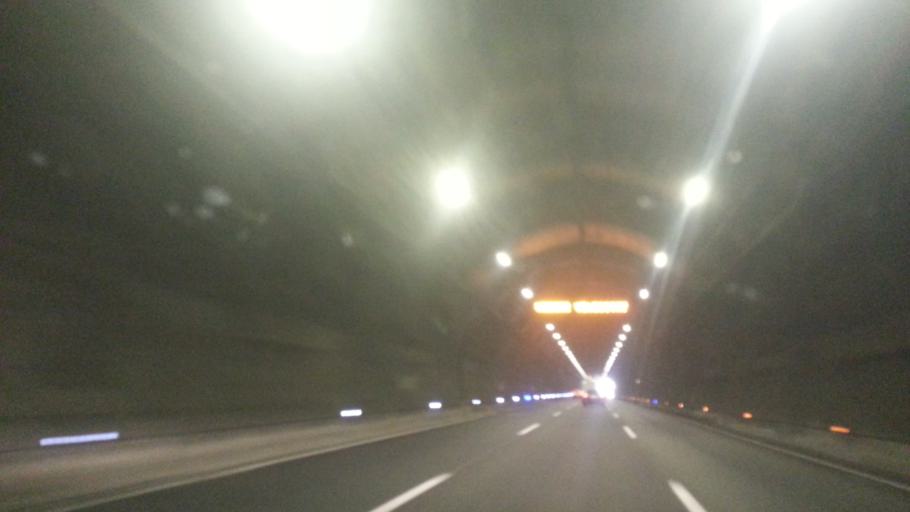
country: ES
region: Catalonia
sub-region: Provincia de Barcelona
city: Castelloli
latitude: 41.5956
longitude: 1.7383
